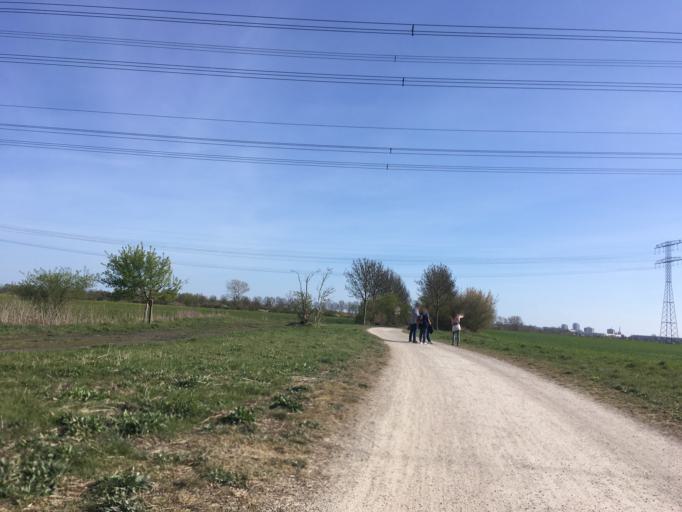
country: DE
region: Berlin
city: Wartenberg
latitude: 52.5948
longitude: 13.5060
